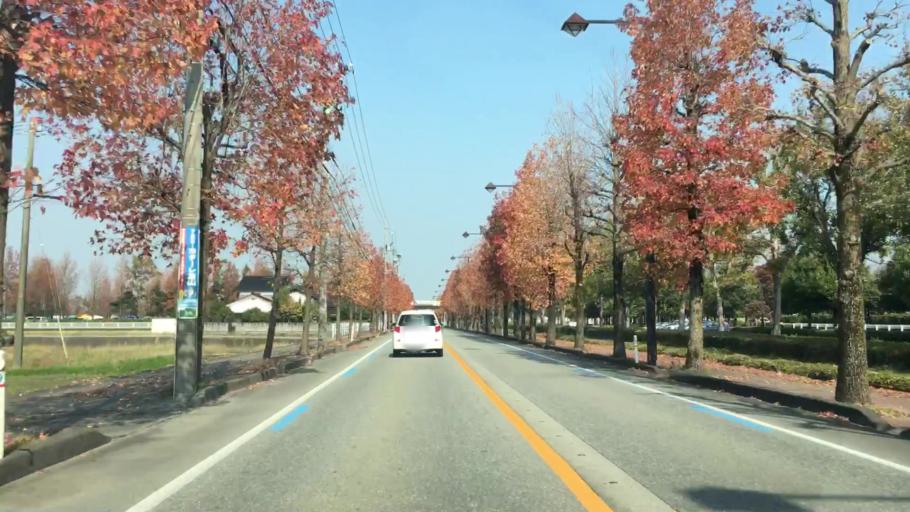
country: JP
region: Toyama
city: Toyama-shi
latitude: 36.6244
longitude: 137.1934
